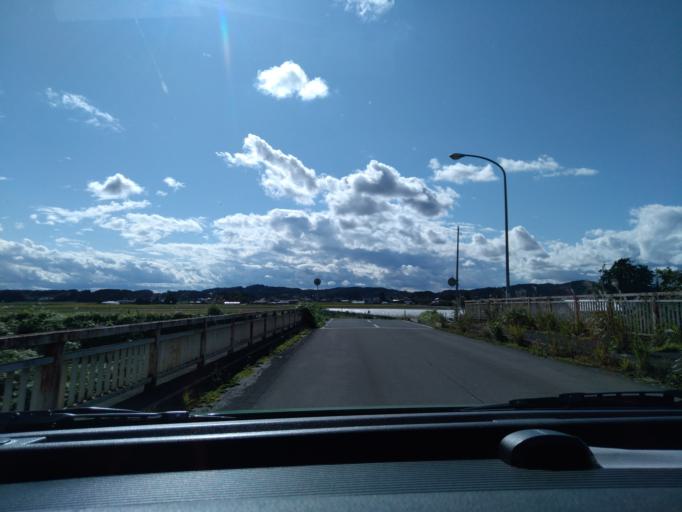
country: JP
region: Iwate
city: Ichinoseki
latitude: 38.7747
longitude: 141.1972
